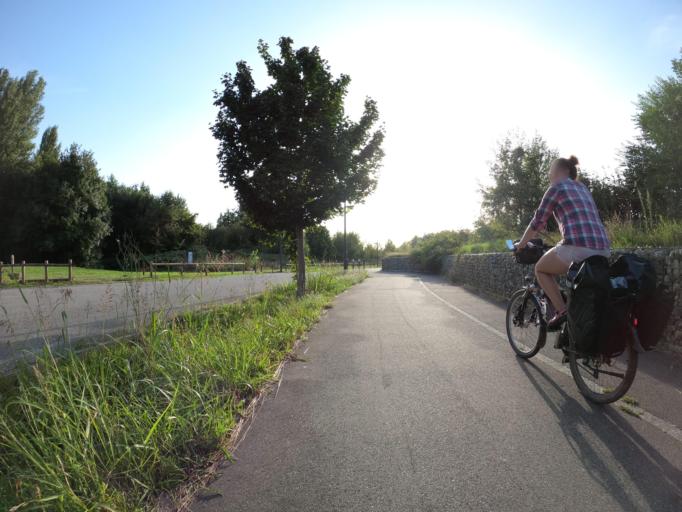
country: FR
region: Midi-Pyrenees
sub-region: Departement de la Haute-Garonne
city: Vieille-Toulouse
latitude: 43.5478
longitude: 1.4289
